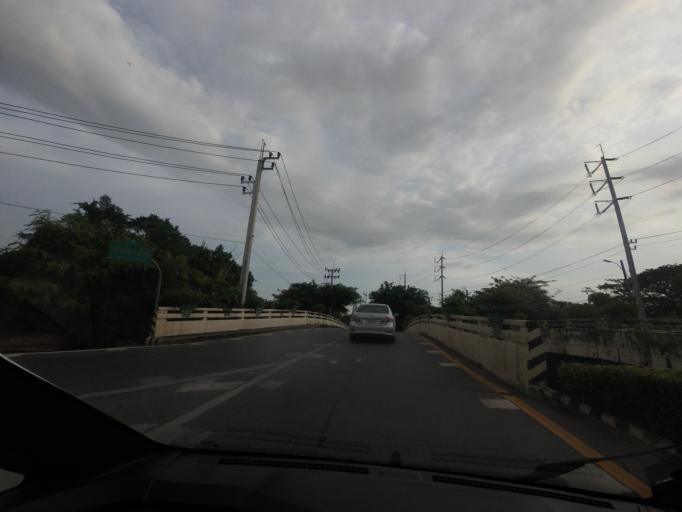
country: TH
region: Bangkok
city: Nong Chok
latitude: 13.8610
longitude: 100.8610
